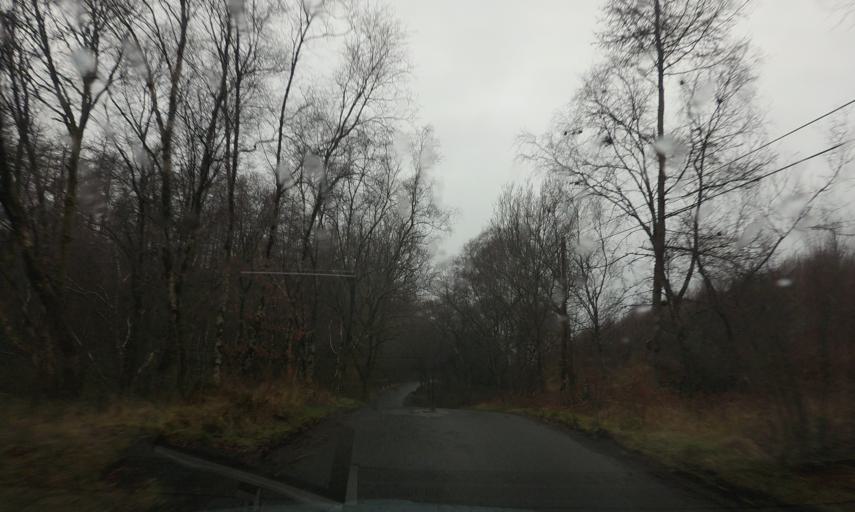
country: GB
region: Scotland
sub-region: West Dunbartonshire
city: Balloch
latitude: 56.1420
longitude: -4.6345
